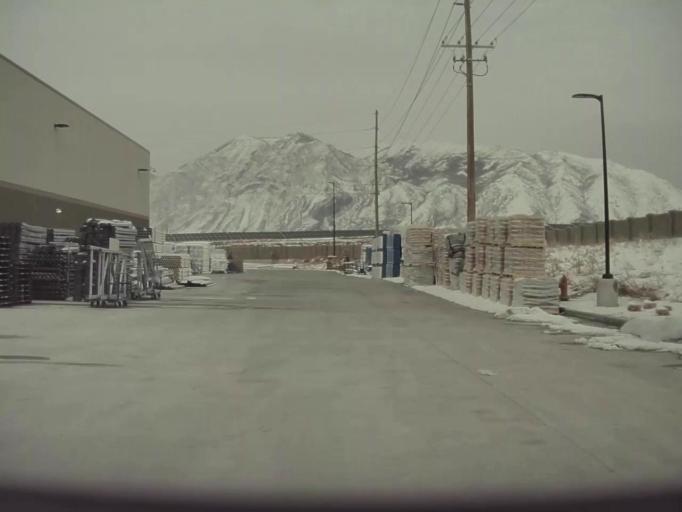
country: US
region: Utah
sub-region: Utah County
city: Spanish Fork
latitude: 40.1265
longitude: -111.6353
